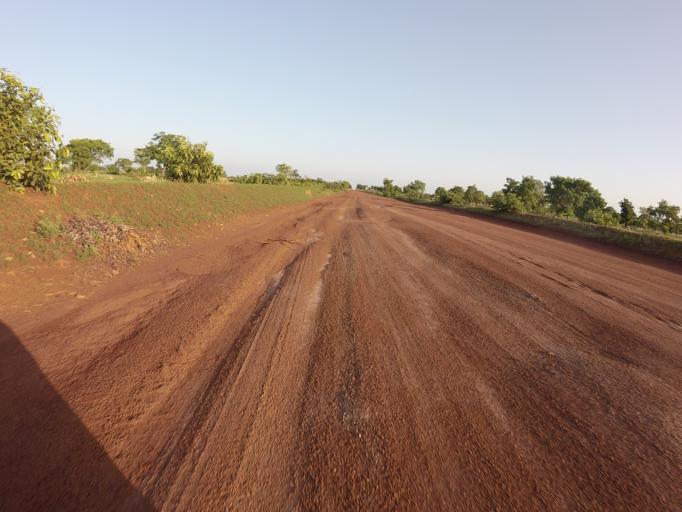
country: TG
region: Savanes
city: Sansanne-Mango
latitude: 10.2707
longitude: -0.0817
